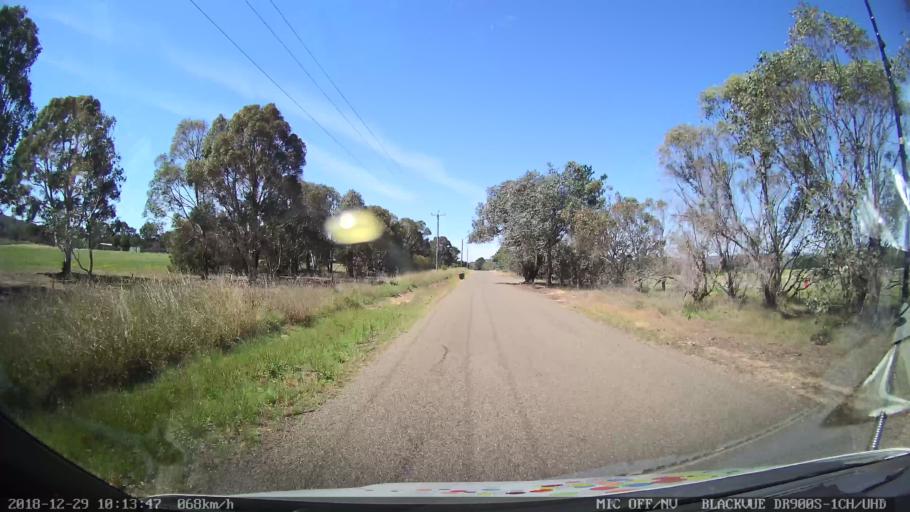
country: AU
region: New South Wales
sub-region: Yass Valley
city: Gundaroo
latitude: -34.9065
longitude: 149.4419
